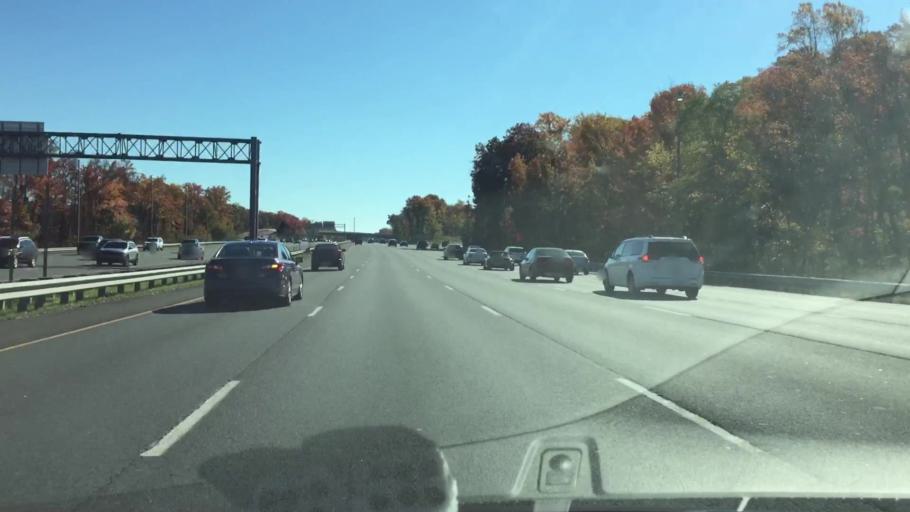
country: US
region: New Jersey
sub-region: Camden County
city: Bellmawr
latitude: 39.8518
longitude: -75.0970
